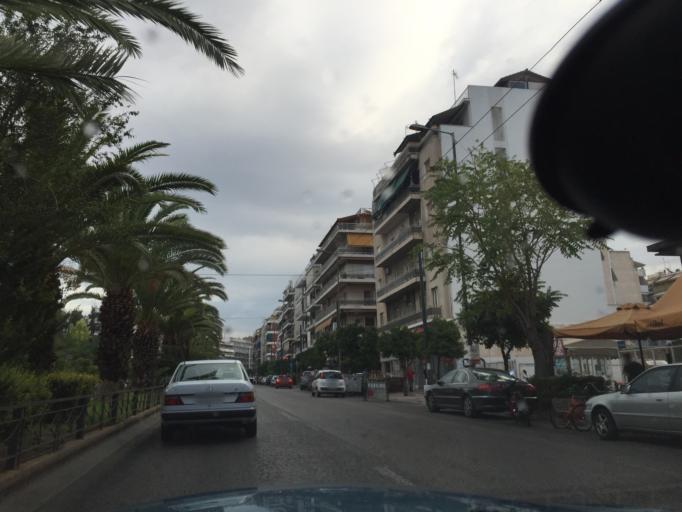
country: GR
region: Attica
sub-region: Nomarchia Athinas
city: Kallithea
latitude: 37.9602
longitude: 23.7083
